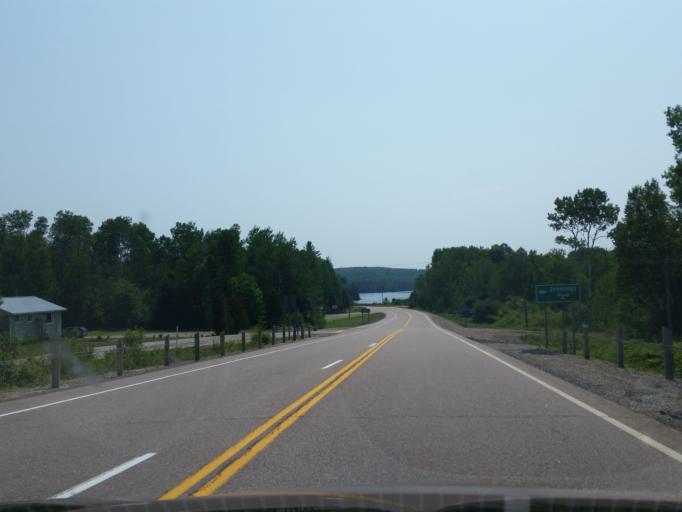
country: CA
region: Ontario
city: Deep River
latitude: 46.1709
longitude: -77.8223
